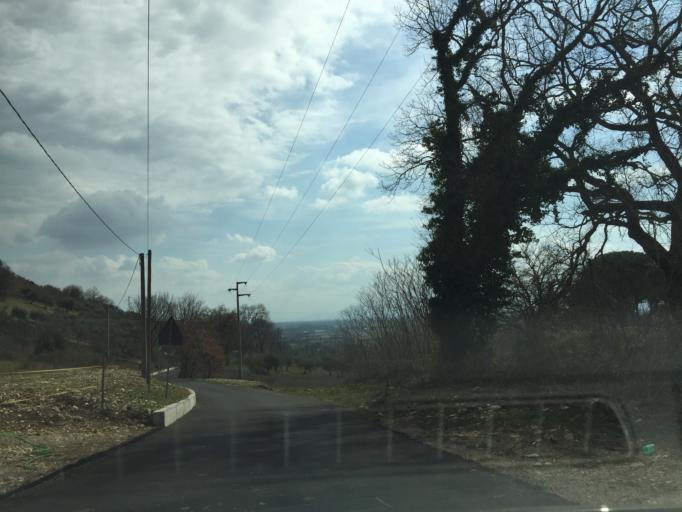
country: IT
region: Latium
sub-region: Provincia di Frosinone
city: Castrocielo
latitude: 41.5234
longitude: 13.7037
